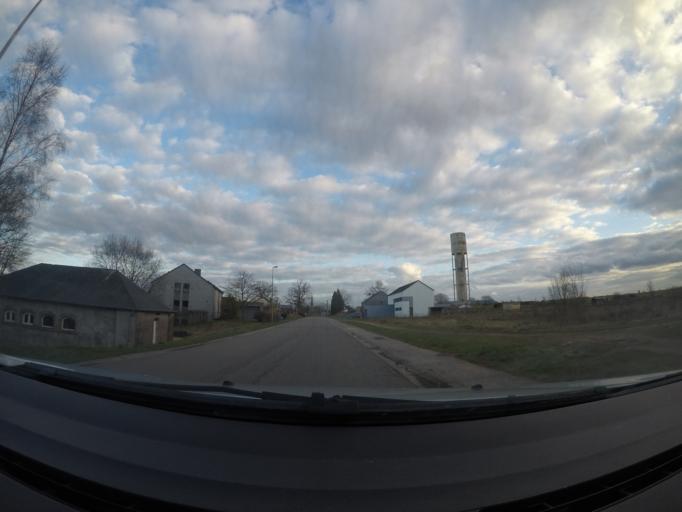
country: BE
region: Wallonia
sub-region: Province du Luxembourg
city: Etalle
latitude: 49.6631
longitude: 5.5711
